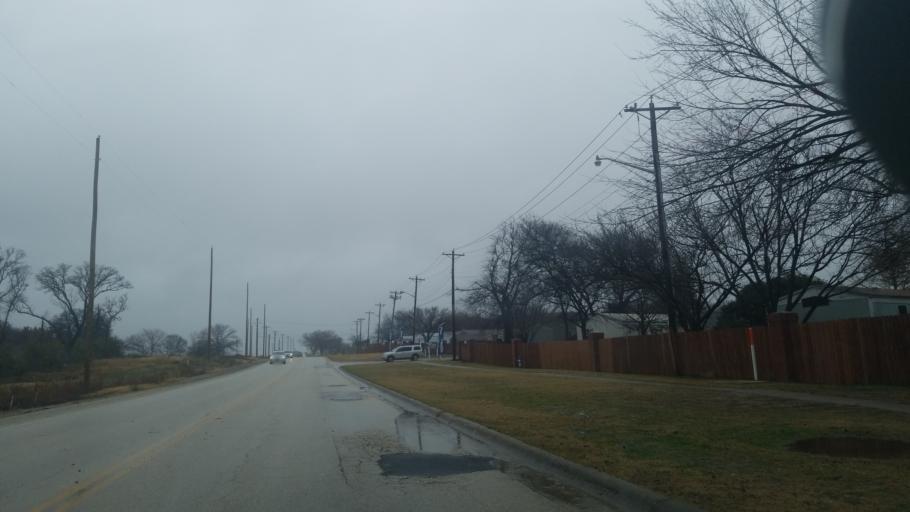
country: US
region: Texas
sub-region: Denton County
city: Corinth
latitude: 33.1814
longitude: -97.0856
